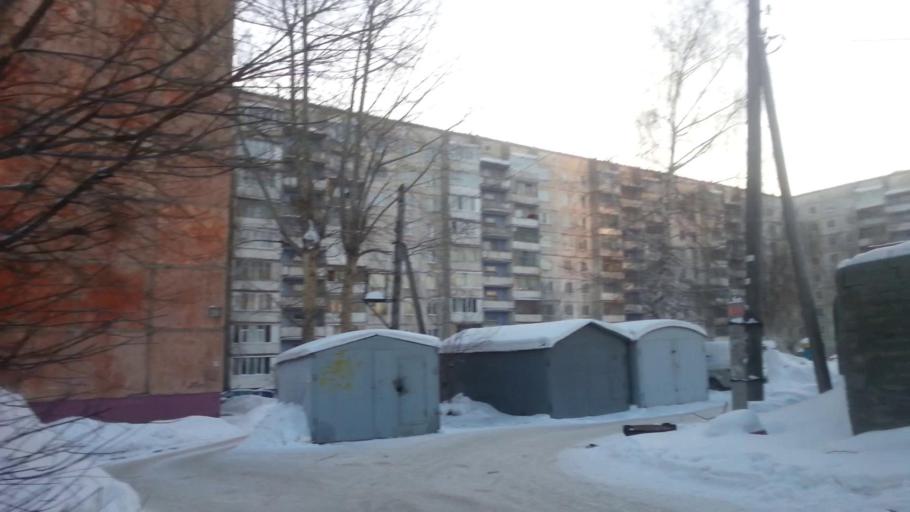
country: RU
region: Altai Krai
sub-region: Gorod Barnaulskiy
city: Barnaul
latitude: 53.3551
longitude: 83.7029
